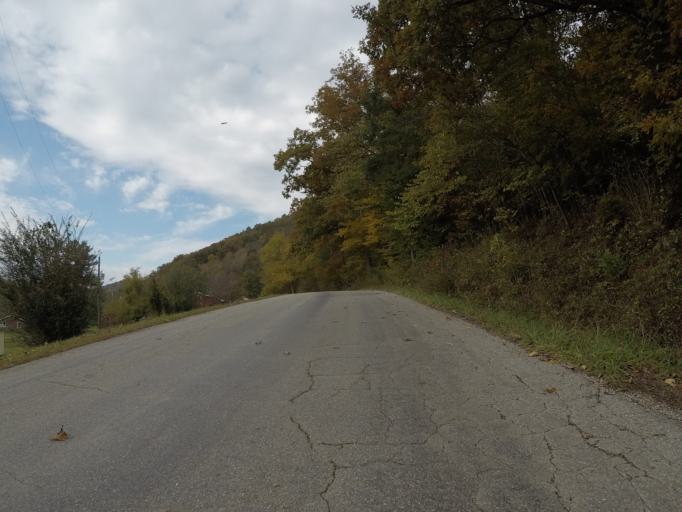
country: US
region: West Virginia
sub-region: Wayne County
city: Lavalette
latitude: 38.3356
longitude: -82.4414
